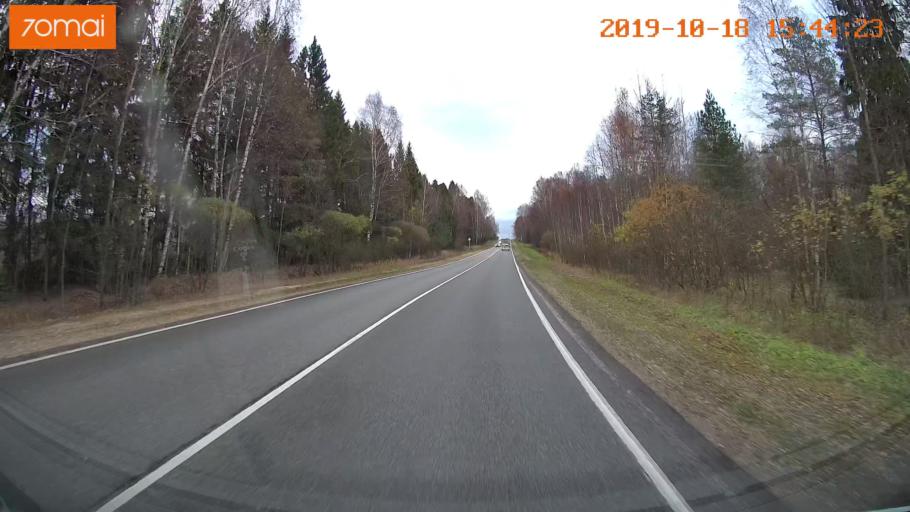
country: RU
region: Vladimir
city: Golovino
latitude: 55.9809
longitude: 40.5492
